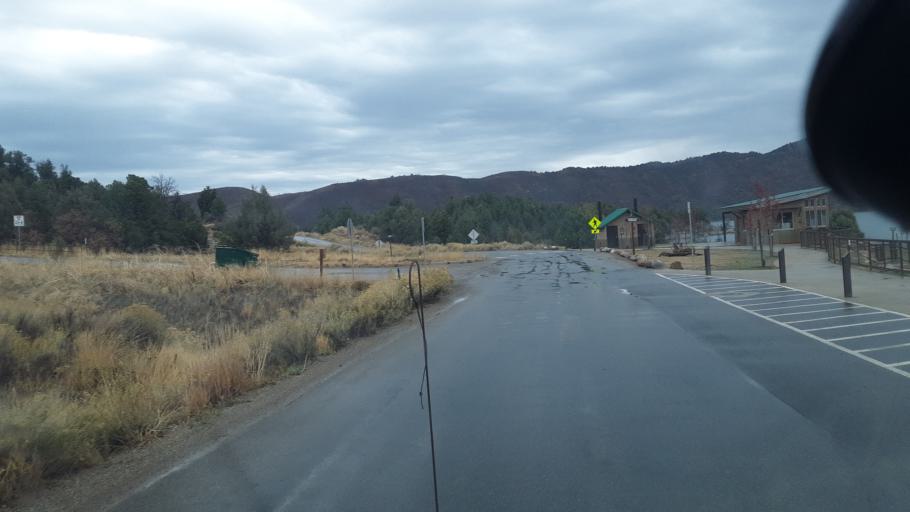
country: US
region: Colorado
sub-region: La Plata County
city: Durango
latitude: 37.2332
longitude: -107.9061
